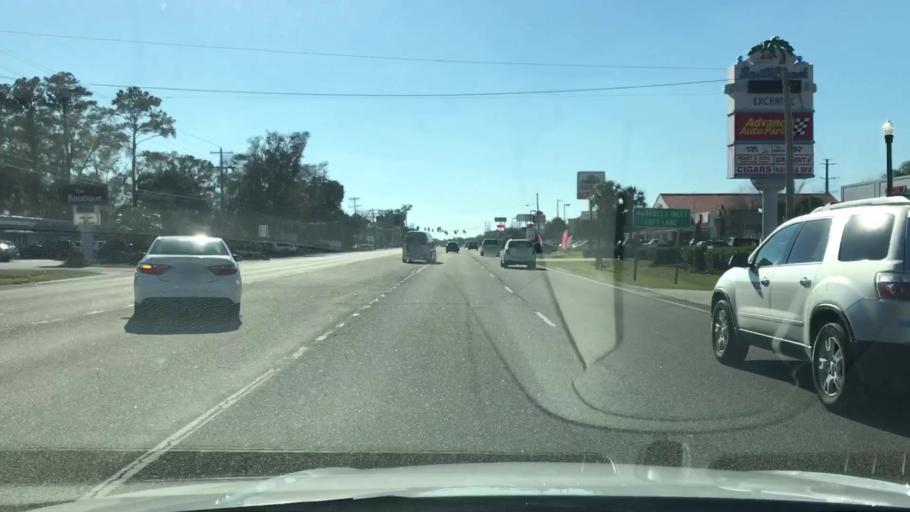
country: US
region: South Carolina
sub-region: Horry County
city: Garden City
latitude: 33.5811
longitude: -79.0192
